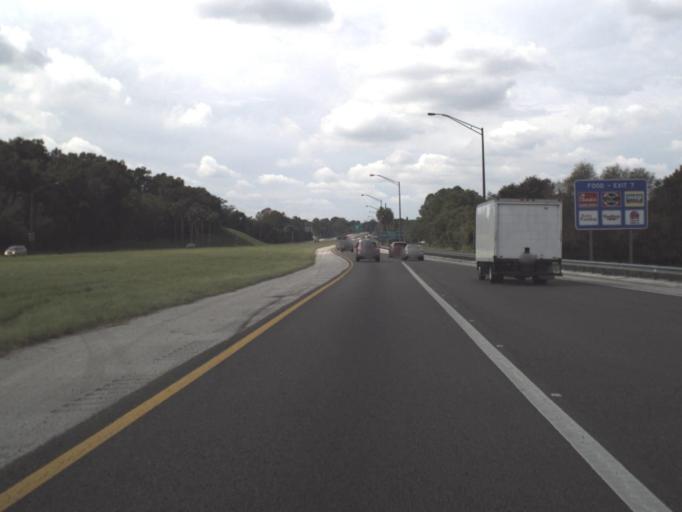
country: US
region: Florida
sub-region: Polk County
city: Lakeland Highlands
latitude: 27.9957
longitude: -81.9370
